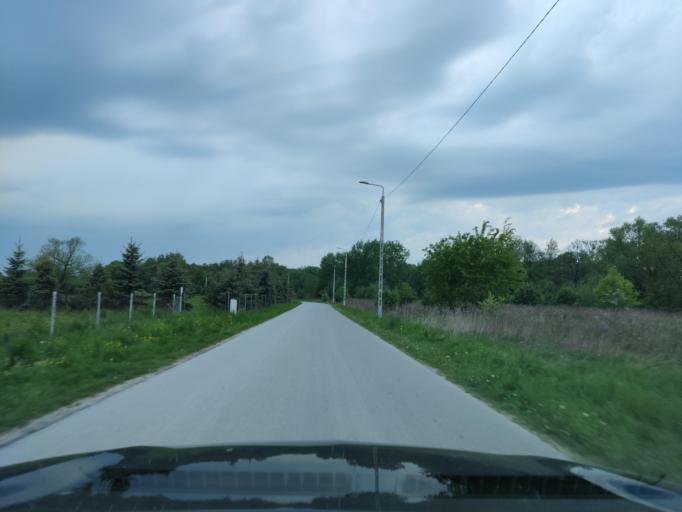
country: PL
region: Masovian Voivodeship
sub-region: Powiat piaseczynski
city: Konstancin-Jeziorna
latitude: 52.1216
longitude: 21.1599
